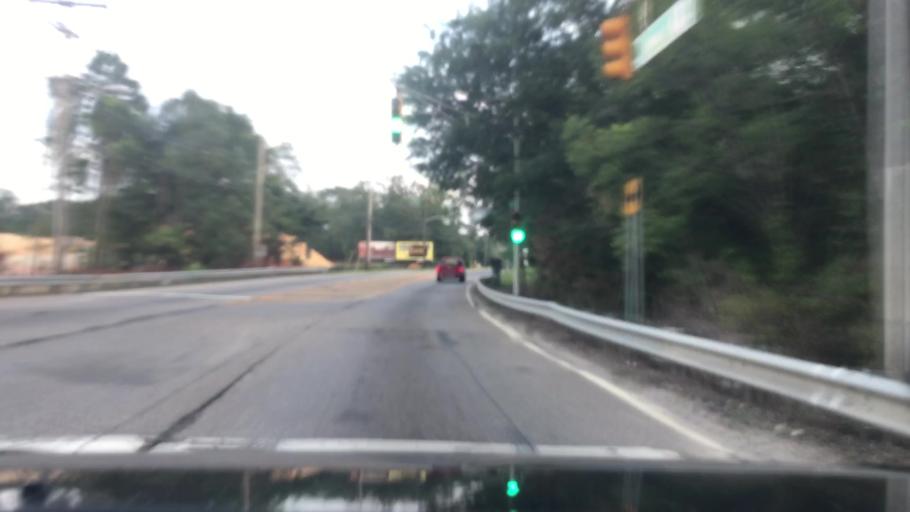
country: US
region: New Jersey
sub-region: Ocean County
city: Silver Ridge
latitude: 40.0003
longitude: -74.2125
